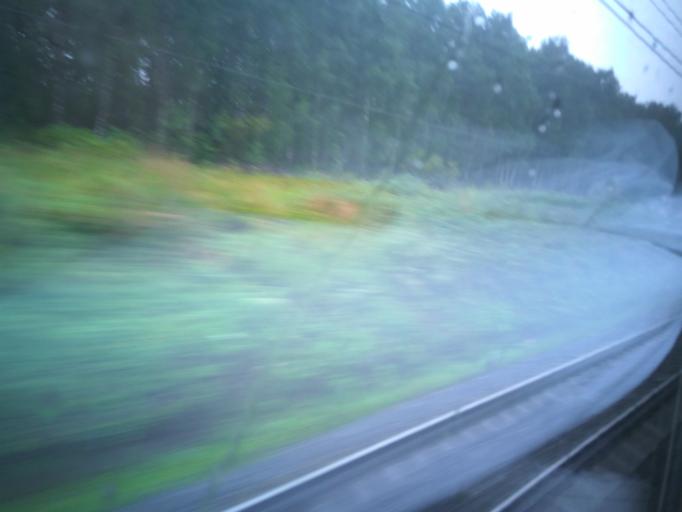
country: RU
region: Moskovskaya
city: Ozherel'ye
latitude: 54.8248
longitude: 38.2547
